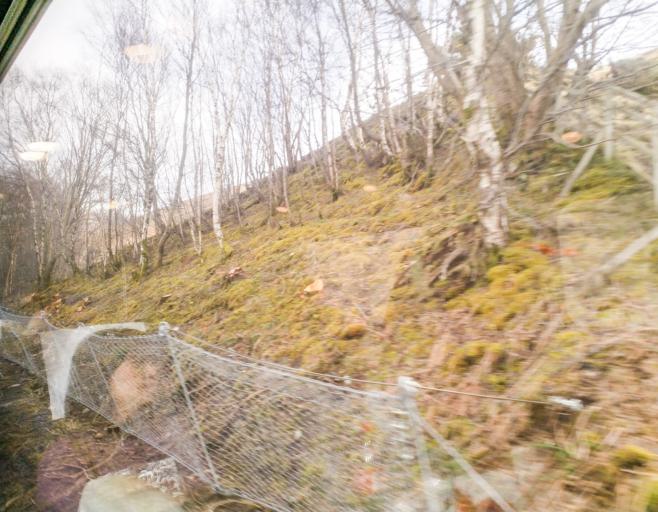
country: GB
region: Scotland
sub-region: Highland
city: Spean Bridge
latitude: 56.8020
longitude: -4.7201
